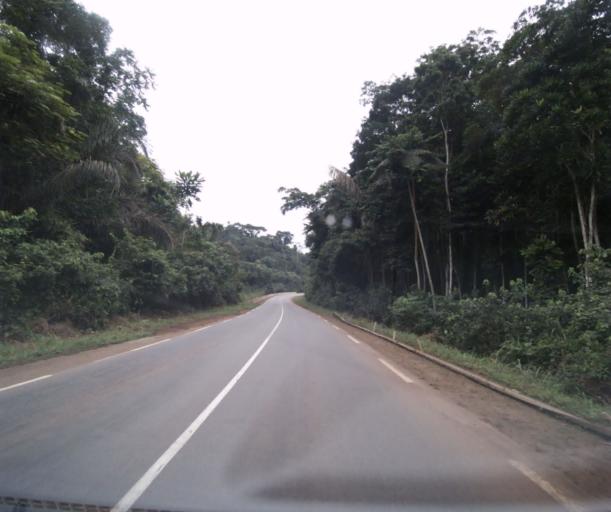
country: CM
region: Centre
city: Mbankomo
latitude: 3.7716
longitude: 11.1723
